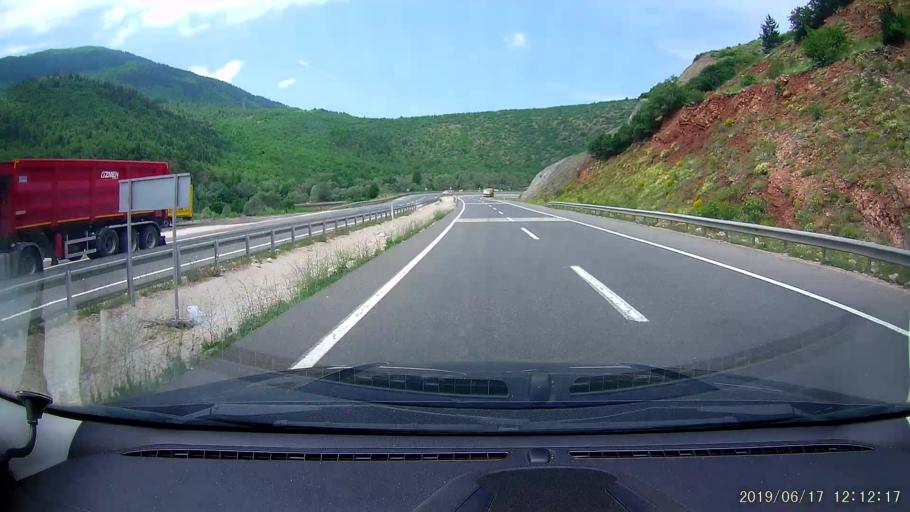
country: TR
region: Karabuk
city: Gozyeri
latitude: 40.8555
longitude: 32.6394
